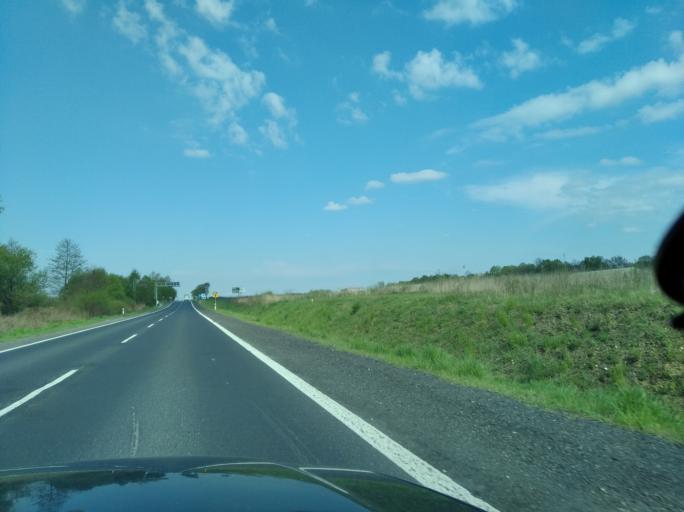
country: PL
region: Subcarpathian Voivodeship
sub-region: Powiat lubaczowski
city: Wielkie Oczy
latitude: 49.9677
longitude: 23.0637
